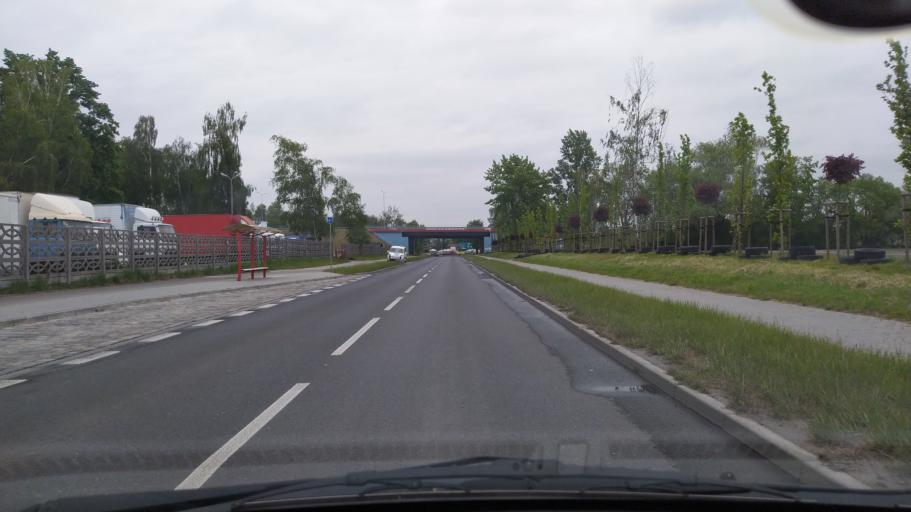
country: PL
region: Silesian Voivodeship
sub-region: Gliwice
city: Gliwice
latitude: 50.2800
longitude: 18.7130
